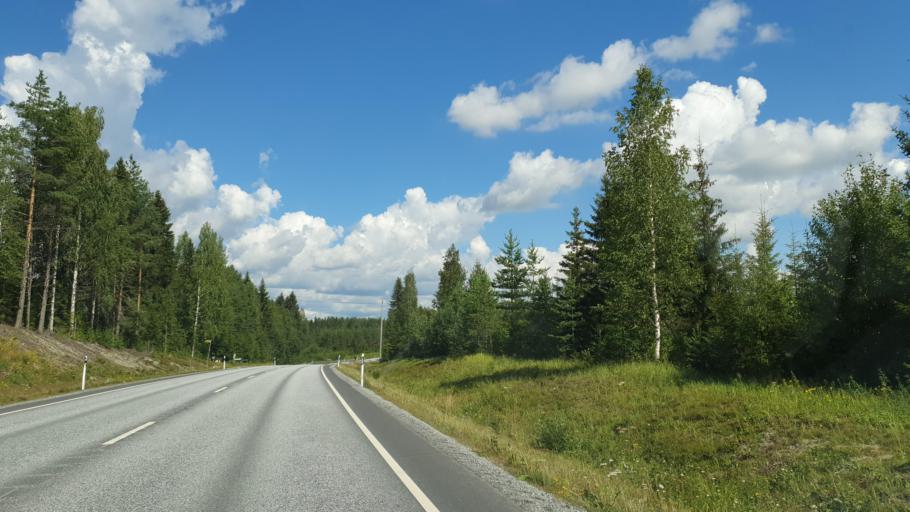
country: FI
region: Northern Savo
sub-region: Ylae-Savo
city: Sonkajaervi
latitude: 63.8330
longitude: 27.4213
